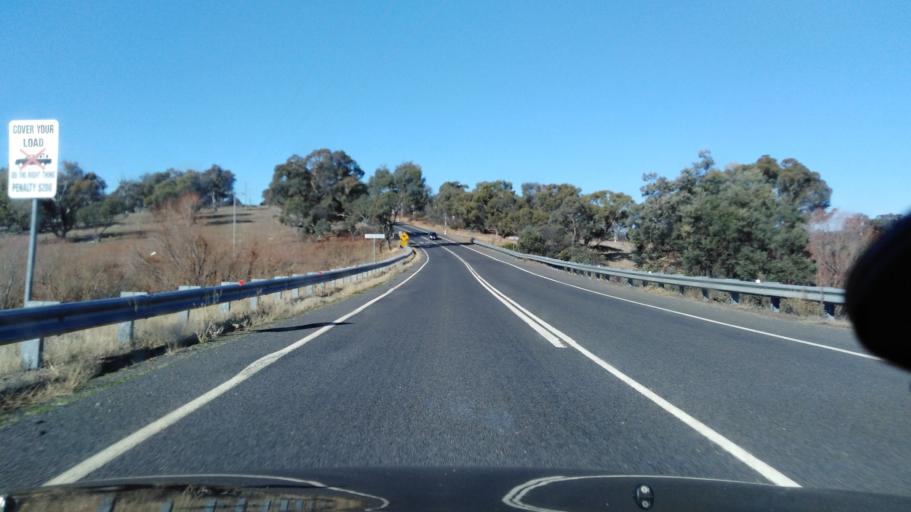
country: AU
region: New South Wales
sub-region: Yass Valley
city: Gundaroo
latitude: -35.1808
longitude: 149.2714
